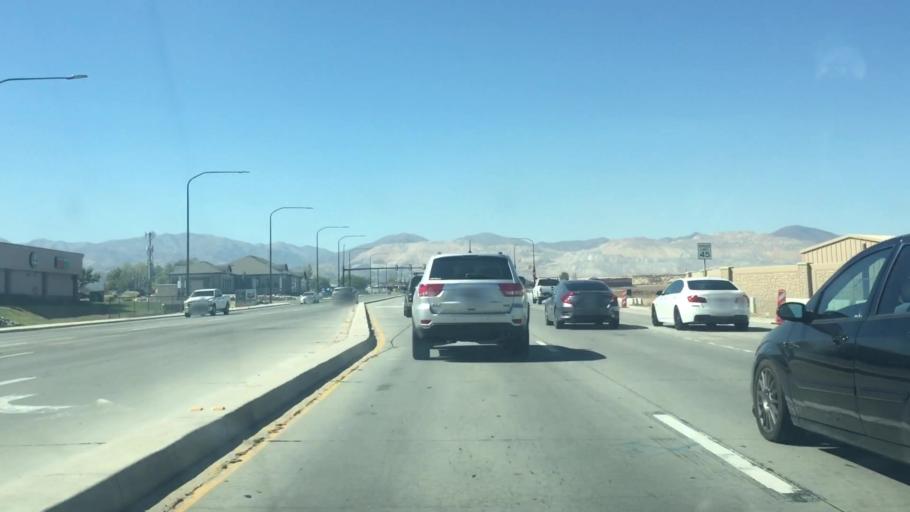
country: US
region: Utah
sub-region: Salt Lake County
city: Riverton
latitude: 40.5083
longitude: -111.9844
